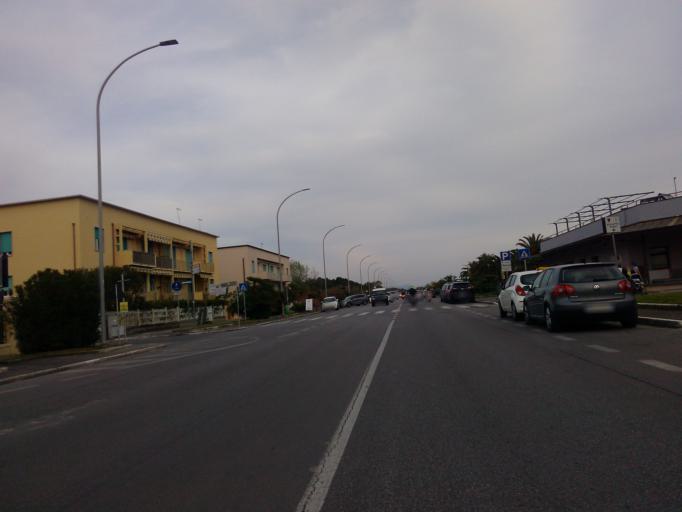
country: IT
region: Tuscany
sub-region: Provincia di Massa-Carrara
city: Massa
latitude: 44.0018
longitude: 10.1088
